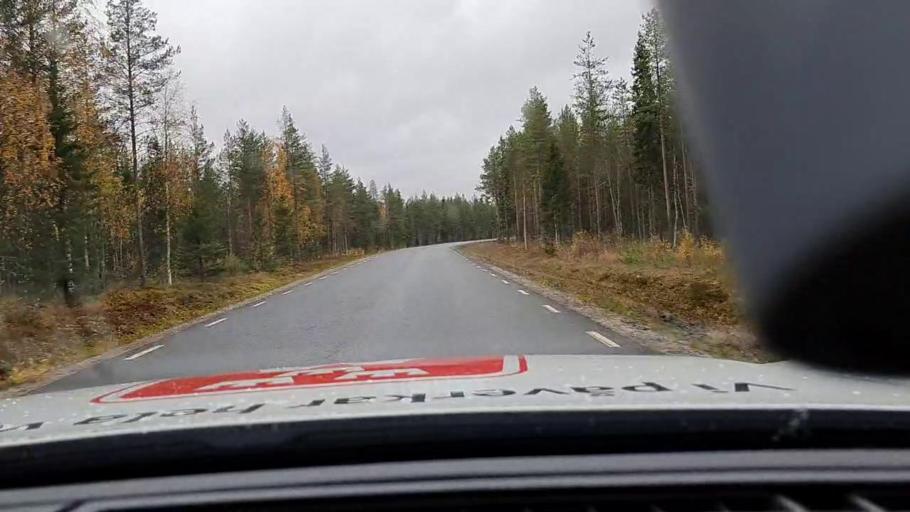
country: SE
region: Norrbotten
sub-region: Haparanda Kommun
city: Haparanda
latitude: 65.9385
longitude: 23.8052
